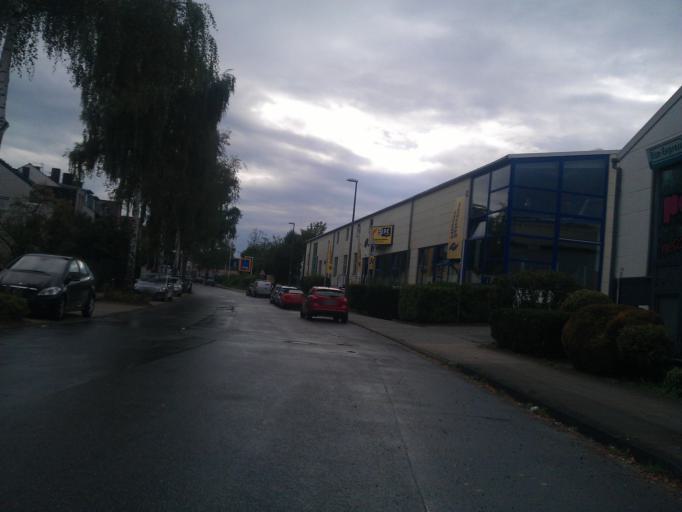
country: DE
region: North Rhine-Westphalia
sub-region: Regierungsbezirk Koln
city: Aachen
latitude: 50.7723
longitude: 6.0629
